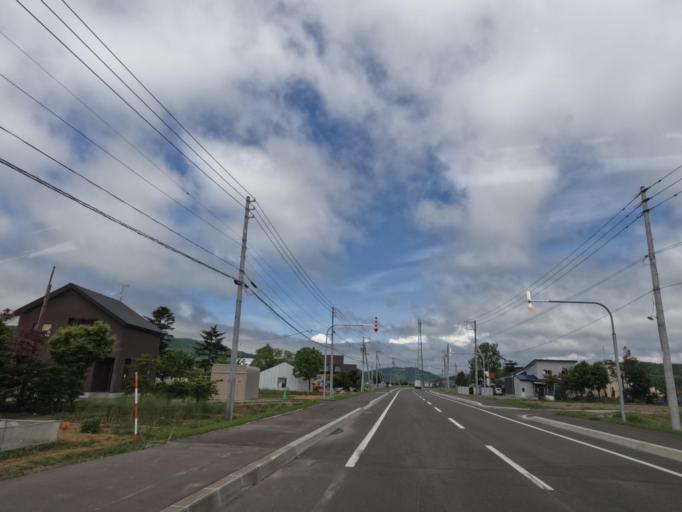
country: JP
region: Hokkaido
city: Tobetsu
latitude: 43.2704
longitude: 141.5297
